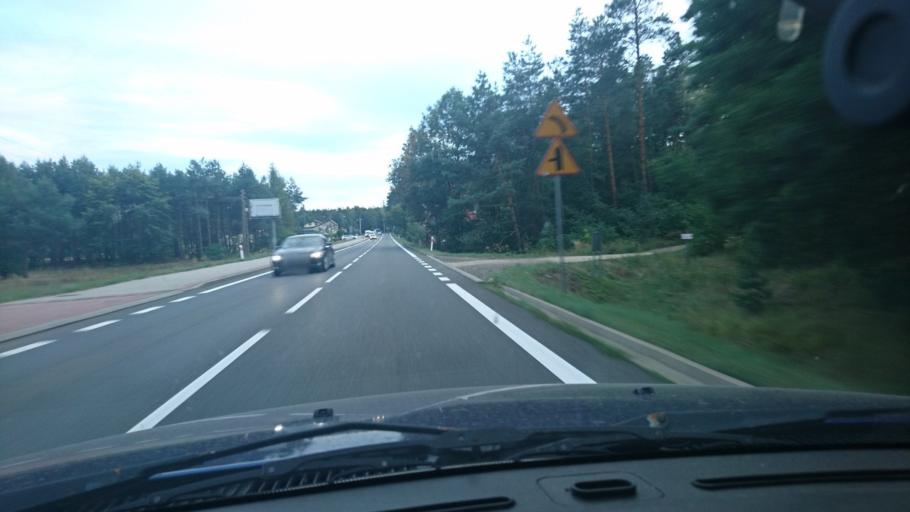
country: PL
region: Silesian Voivodeship
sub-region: Powiat tarnogorski
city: Tworog
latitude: 50.5943
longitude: 18.7016
